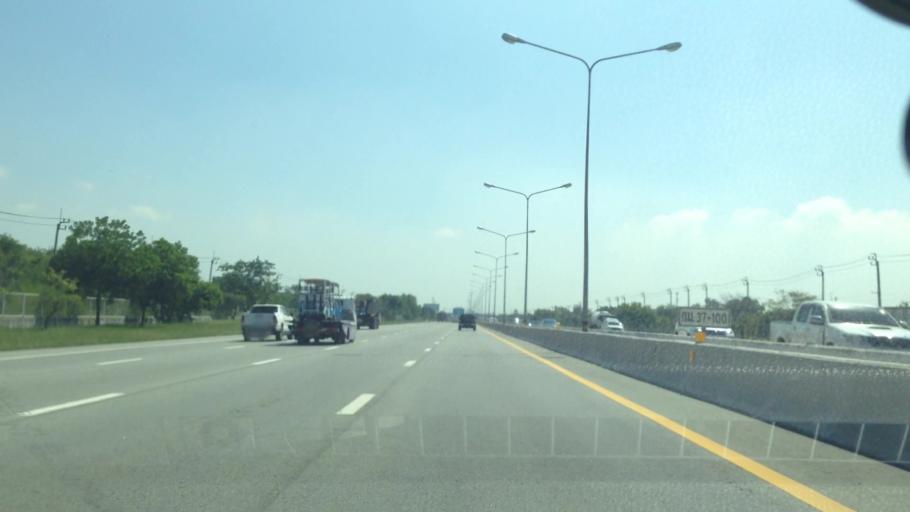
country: TH
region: Chachoengsao
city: Bang Pakong
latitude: 13.6136
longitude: 100.9270
